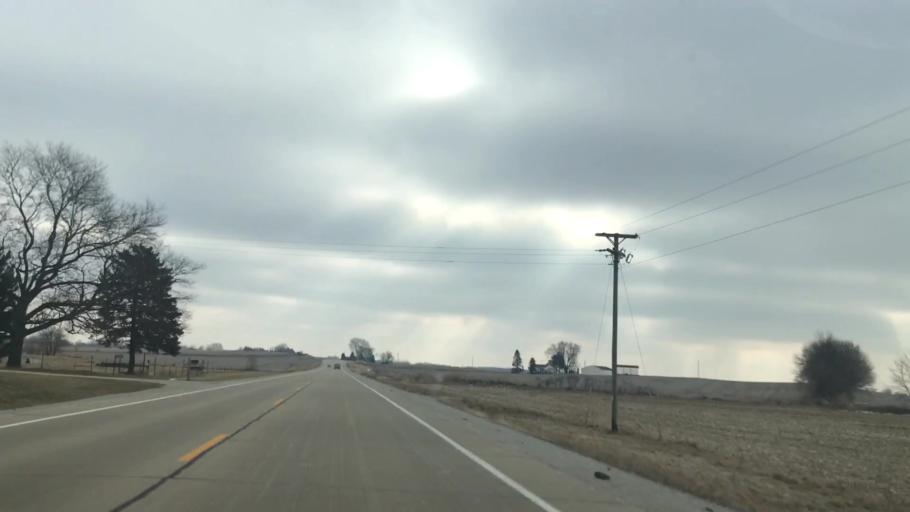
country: US
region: Wisconsin
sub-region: Dodge County
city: Beaver Dam
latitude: 43.4818
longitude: -88.7849
